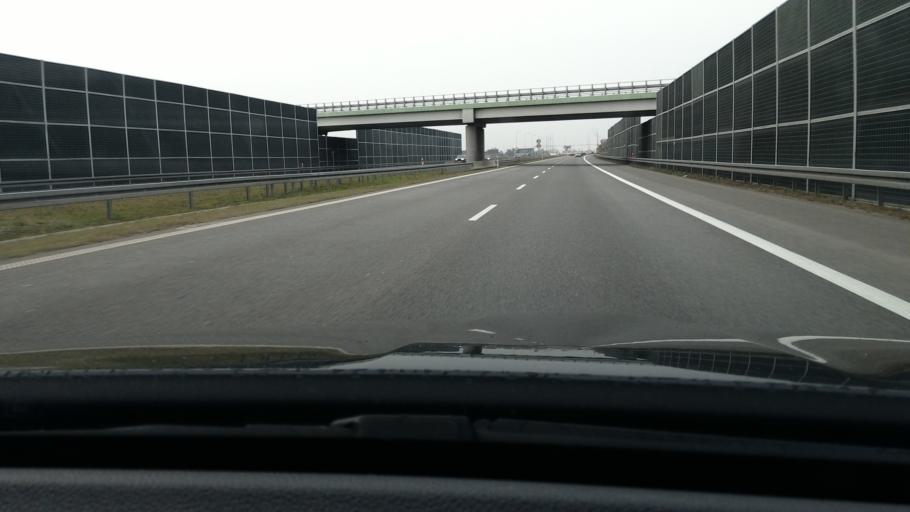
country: PL
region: Masovian Voivodeship
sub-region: Powiat pruszkowski
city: Brwinow
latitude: 52.1674
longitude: 20.7414
